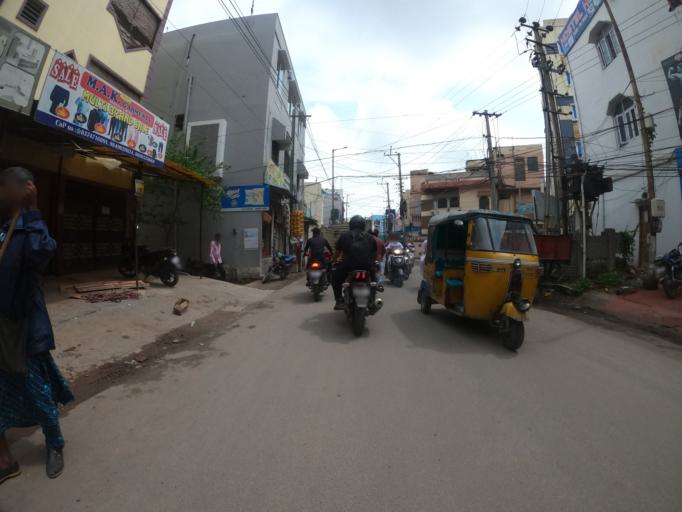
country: IN
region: Telangana
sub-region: Hyderabad
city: Hyderabad
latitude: 17.3963
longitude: 78.4175
